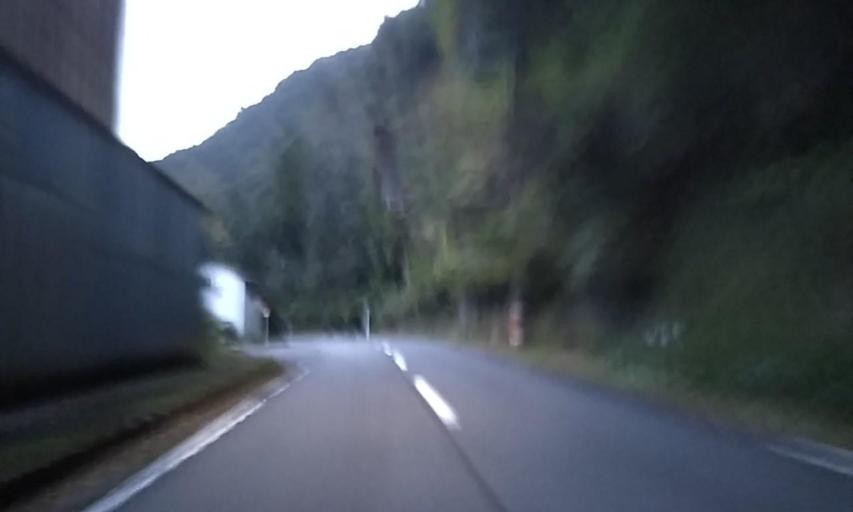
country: JP
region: Wakayama
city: Shingu
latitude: 33.7419
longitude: 135.9338
